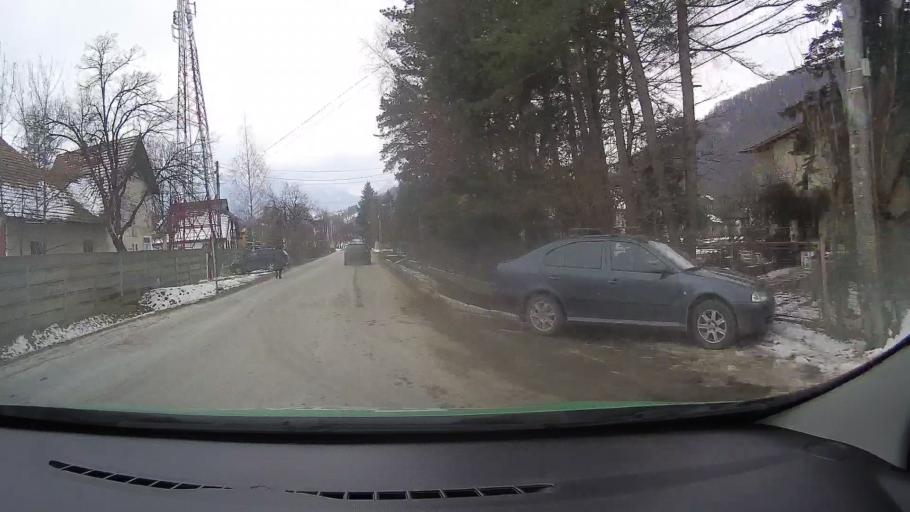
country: RO
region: Brasov
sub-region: Comuna Bran
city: Bran
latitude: 45.5239
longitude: 25.3655
